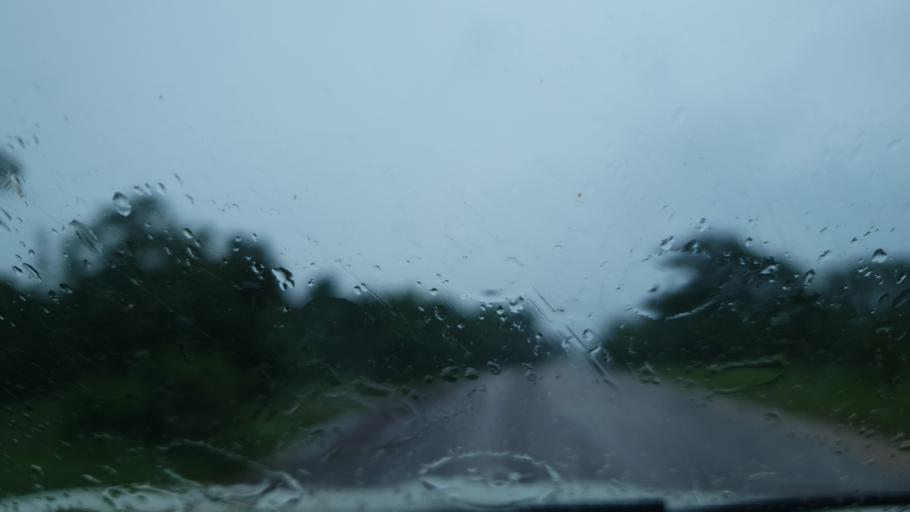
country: ML
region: Sikasso
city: Kolondieba
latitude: 11.6181
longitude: -6.6785
